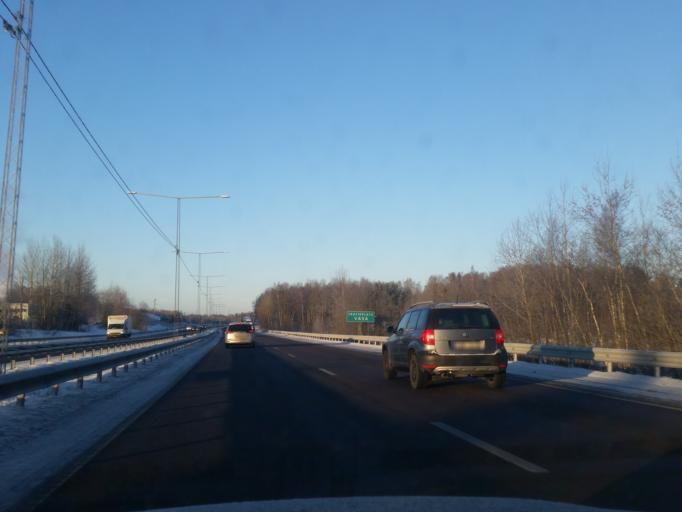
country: SE
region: Stockholm
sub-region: Sodertalje Kommun
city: Soedertaelje
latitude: 59.1832
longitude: 17.5862
